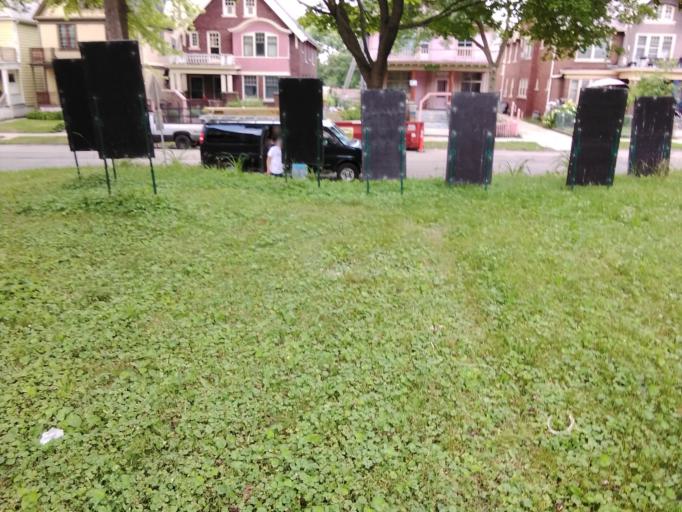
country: US
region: Wisconsin
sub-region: Milwaukee County
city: Milwaukee
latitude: 43.0665
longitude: -87.9109
